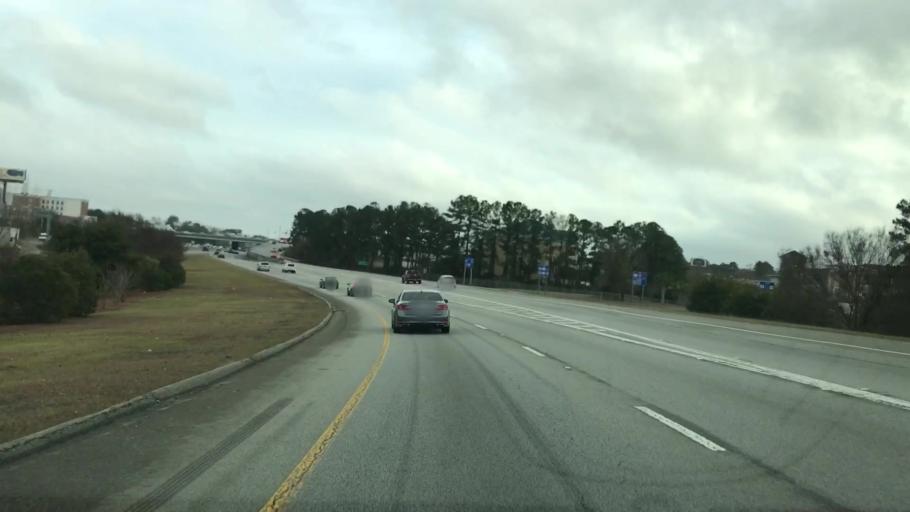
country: US
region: South Carolina
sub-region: Berkeley County
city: Hanahan
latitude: 32.9391
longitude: -80.0506
